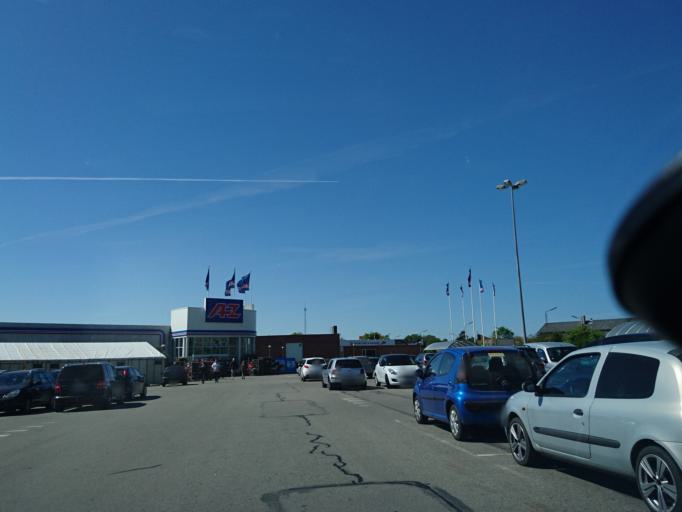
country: DK
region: North Denmark
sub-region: Hjorring Kommune
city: Hjorring
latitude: 57.4452
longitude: 10.0040
